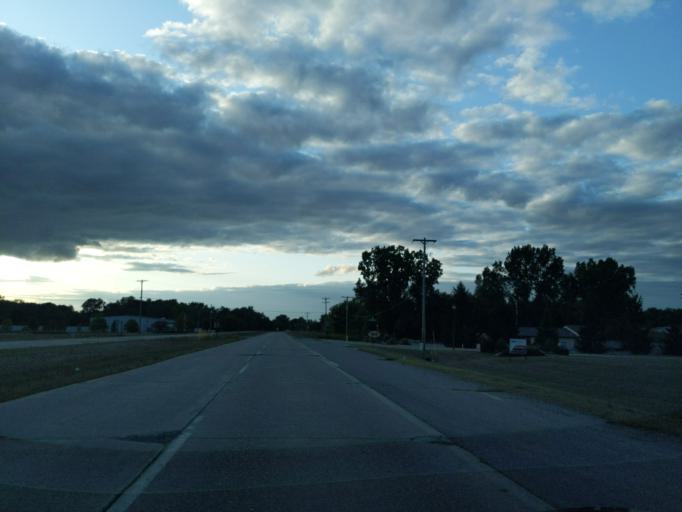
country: US
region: Michigan
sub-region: Ingham County
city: Holt
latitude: 42.6120
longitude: -84.4911
